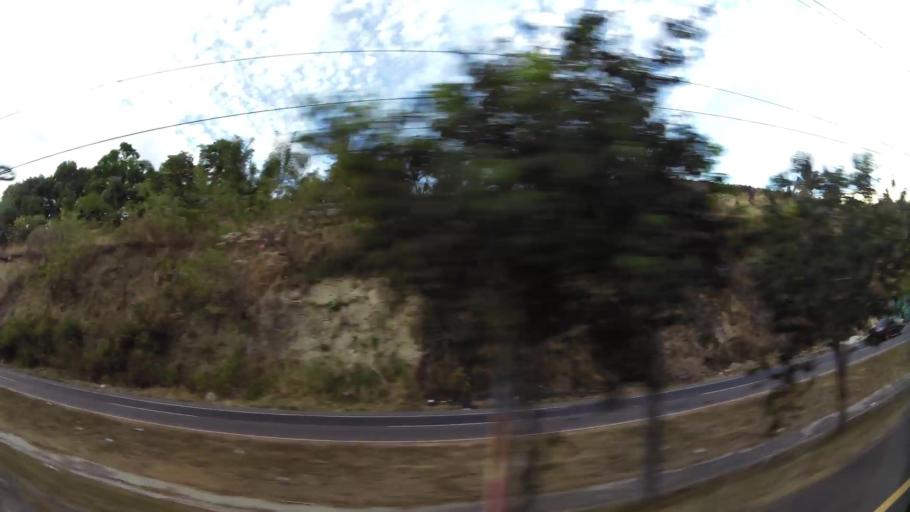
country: SV
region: San Vicente
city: Apastepeque
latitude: 13.6701
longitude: -88.8317
